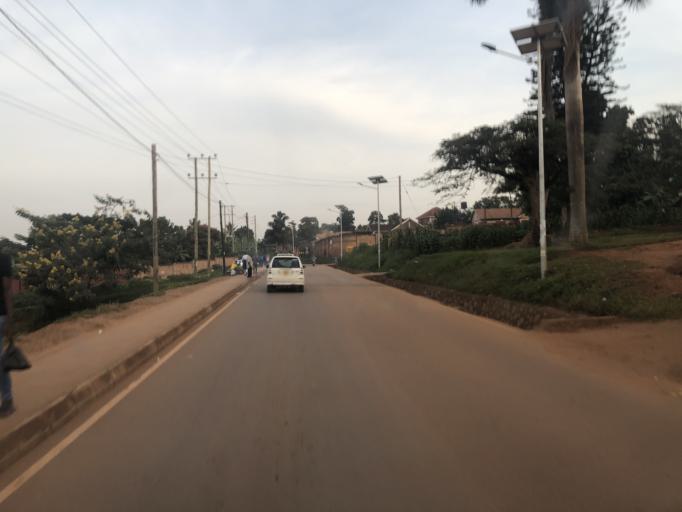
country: UG
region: Central Region
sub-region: Kampala District
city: Kampala
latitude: 0.2747
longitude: 32.5438
